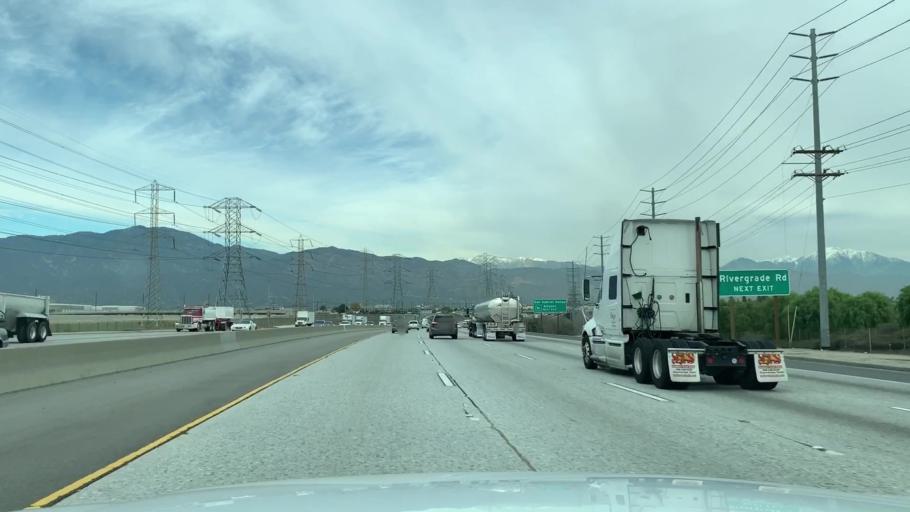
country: US
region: California
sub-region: Los Angeles County
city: Mayflower Village
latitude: 34.0868
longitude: -117.9957
